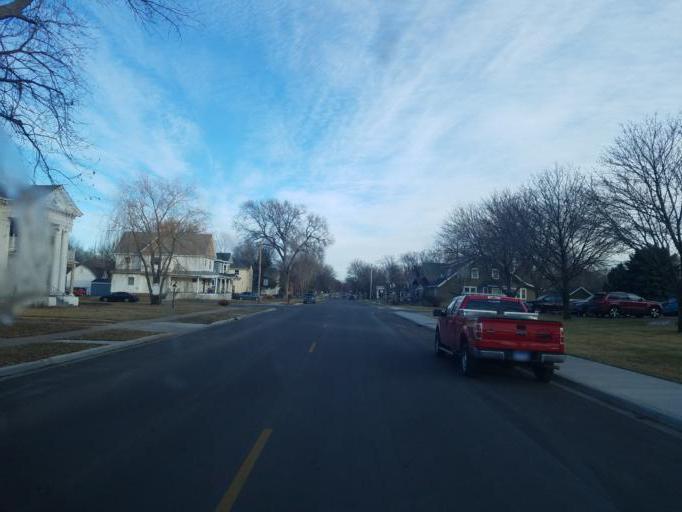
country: US
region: South Dakota
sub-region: Davison County
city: Mitchell
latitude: 43.7135
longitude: -98.0236
